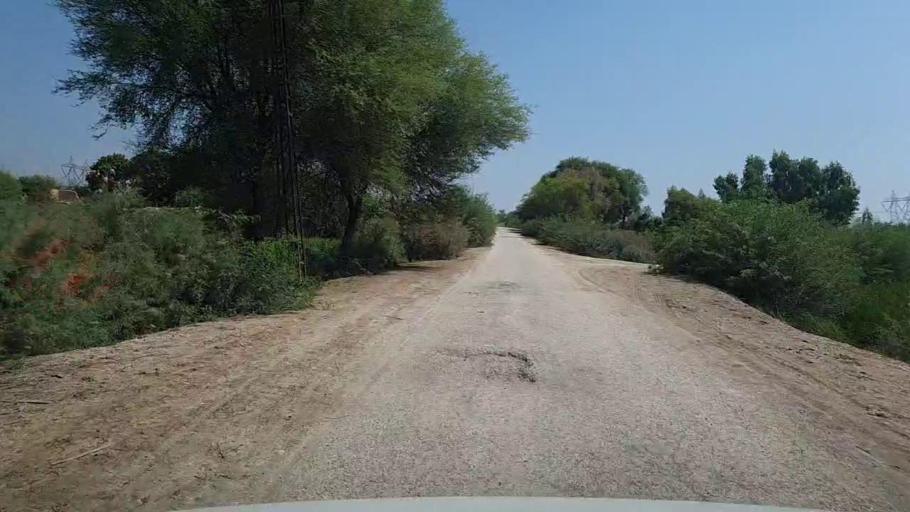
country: PK
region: Sindh
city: Kandhkot
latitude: 28.2889
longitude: 69.3531
